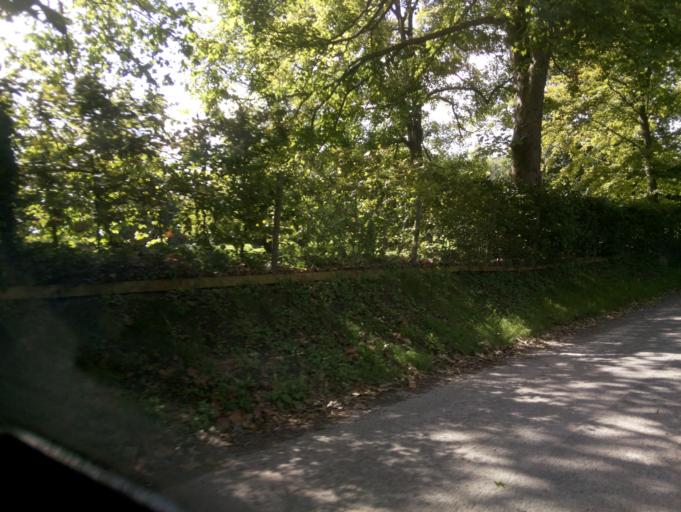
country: GB
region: England
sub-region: Wiltshire
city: Erlestoke
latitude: 51.2856
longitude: -2.0702
